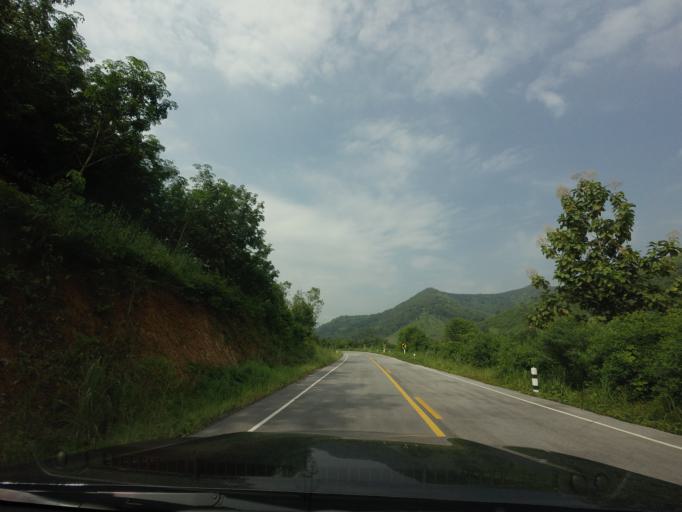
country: TH
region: Loei
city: Chiang Khan
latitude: 17.7851
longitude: 101.5484
